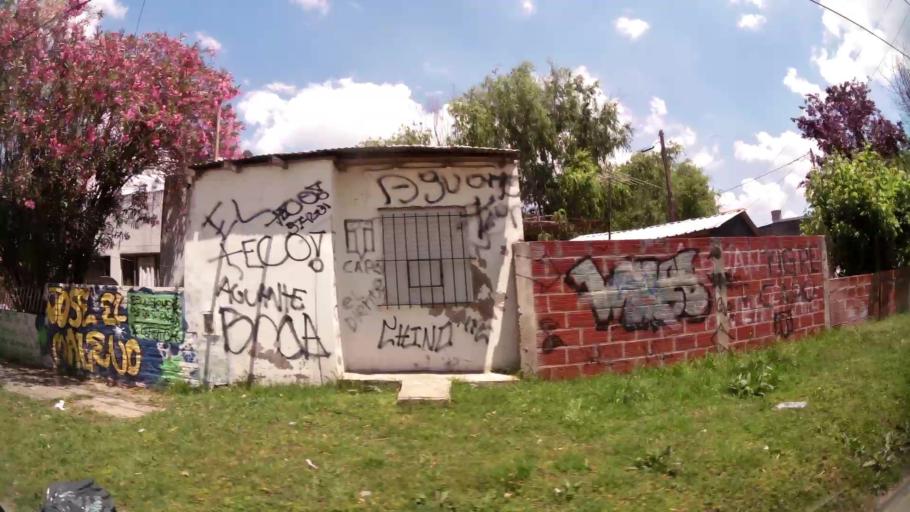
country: AR
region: Buenos Aires
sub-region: Partido de Tigre
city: Tigre
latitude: -34.4101
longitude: -58.5968
